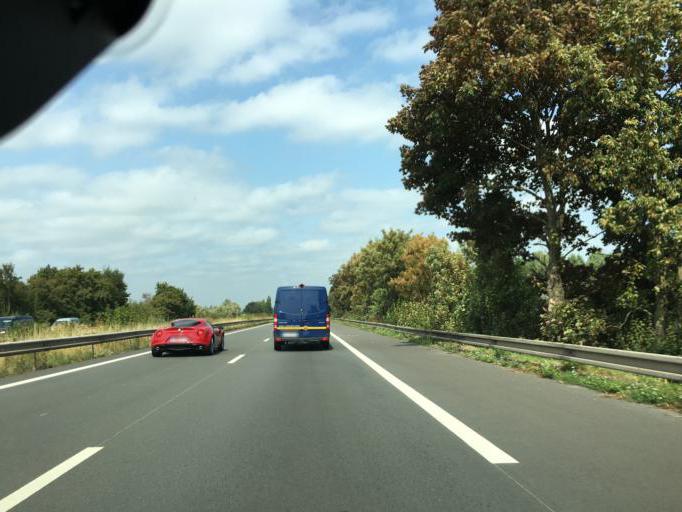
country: FR
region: Nord-Pas-de-Calais
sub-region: Departement du Nord
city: Quarouble
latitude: 50.3919
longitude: 3.6137
